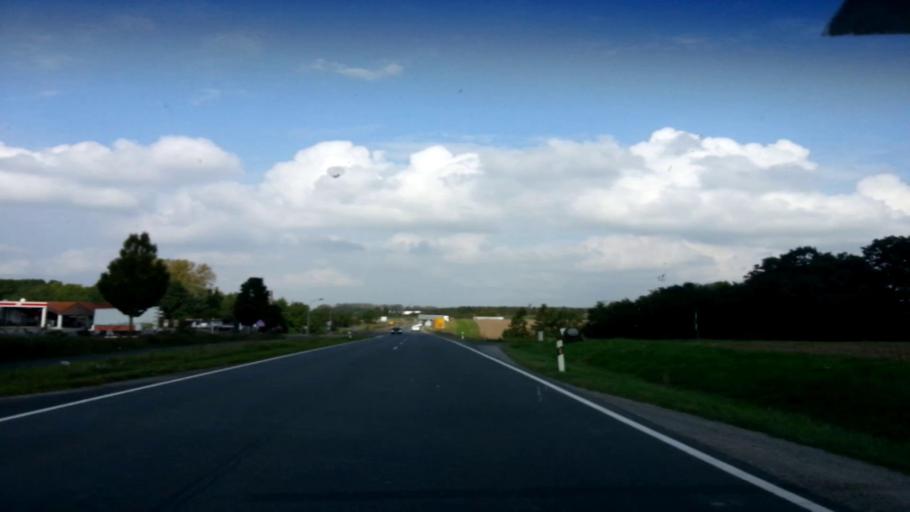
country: DE
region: Bavaria
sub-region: Regierungsbezirk Unterfranken
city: Castell
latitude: 49.7694
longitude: 10.3414
